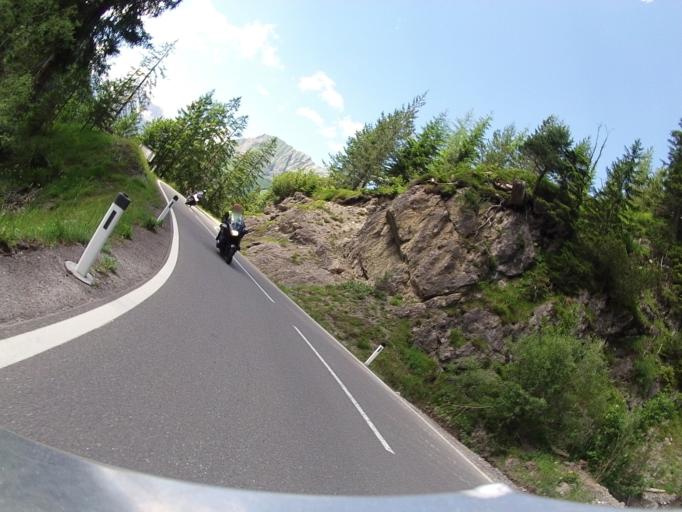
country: AT
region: Tyrol
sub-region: Politischer Bezirk Reutte
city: Gramais
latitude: 47.2953
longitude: 10.6027
